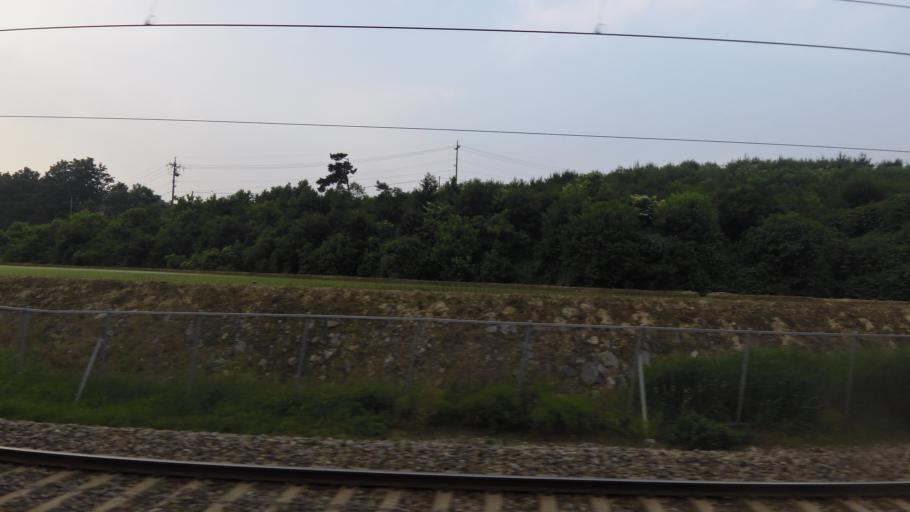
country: KR
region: Daejeon
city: Songgang-dong
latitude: 36.5422
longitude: 127.3364
